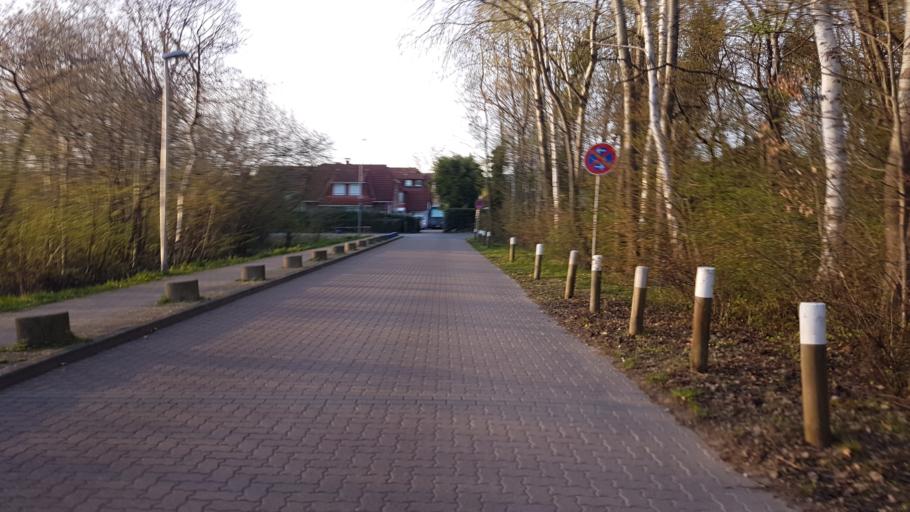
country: DE
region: Lower Saxony
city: Isernhagen Farster Bauerschaft
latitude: 52.4295
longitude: 9.8593
